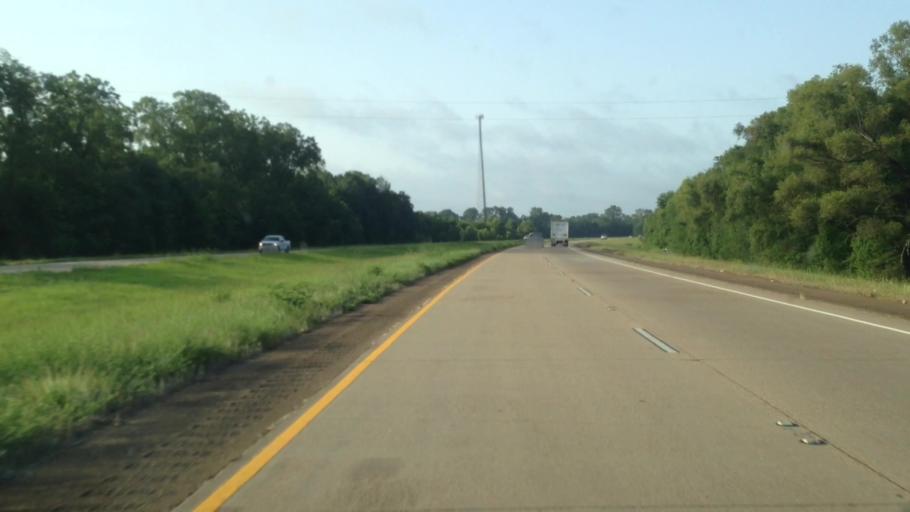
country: US
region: Louisiana
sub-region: Rapides Parish
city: Lecompte
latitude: 31.1257
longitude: -92.4430
